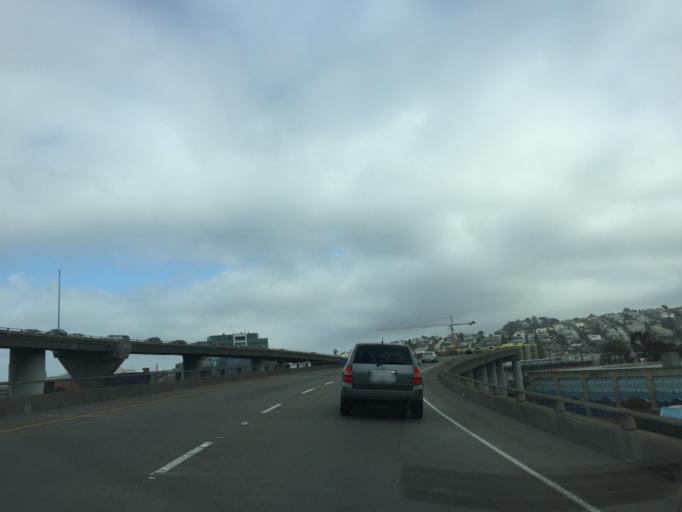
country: US
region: California
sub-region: San Francisco County
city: San Francisco
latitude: 37.7723
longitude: -122.3985
